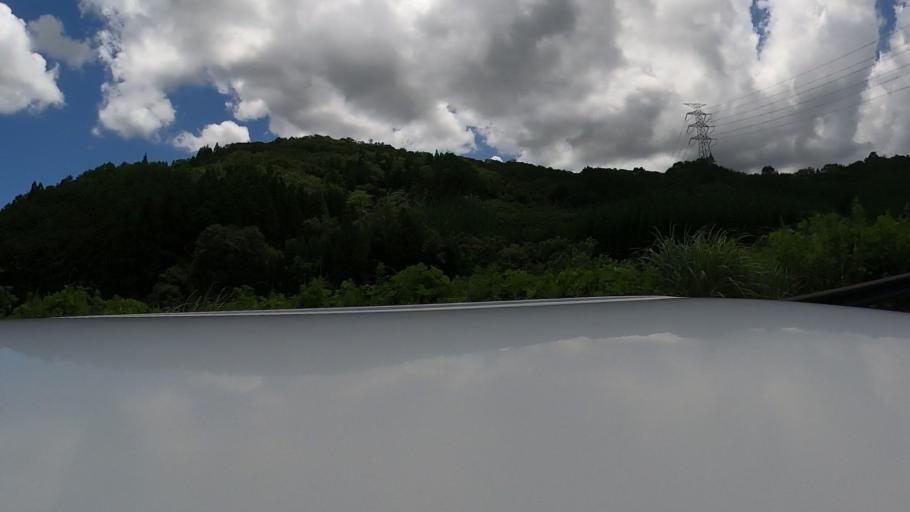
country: JP
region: Miyazaki
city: Nobeoka
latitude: 32.5784
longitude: 131.5218
